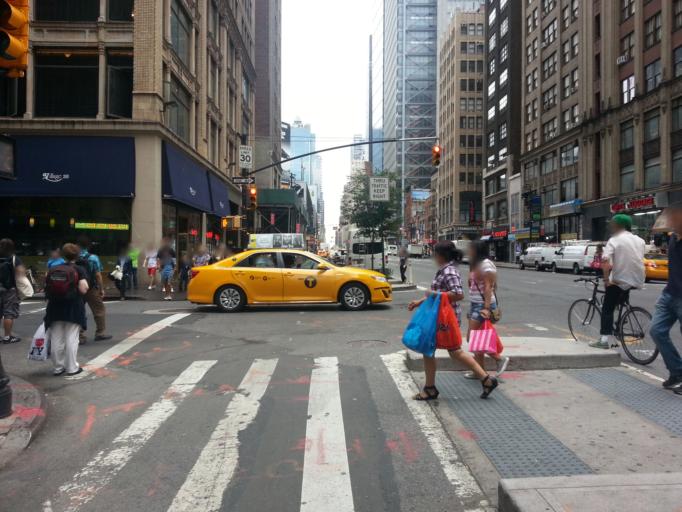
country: US
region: New Jersey
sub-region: Hudson County
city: Weehawken
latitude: 40.7546
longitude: -73.9918
